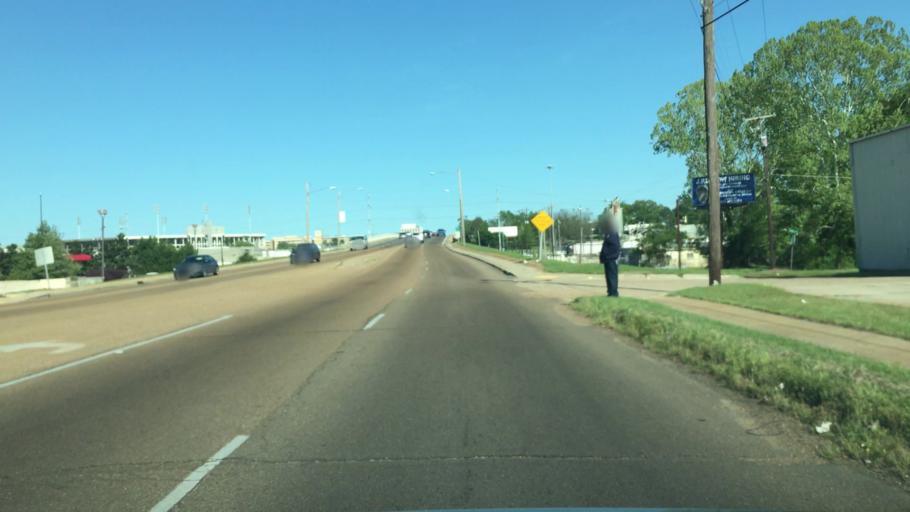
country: US
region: Mississippi
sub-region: Hinds County
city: Jackson
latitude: 32.3268
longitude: -90.1905
